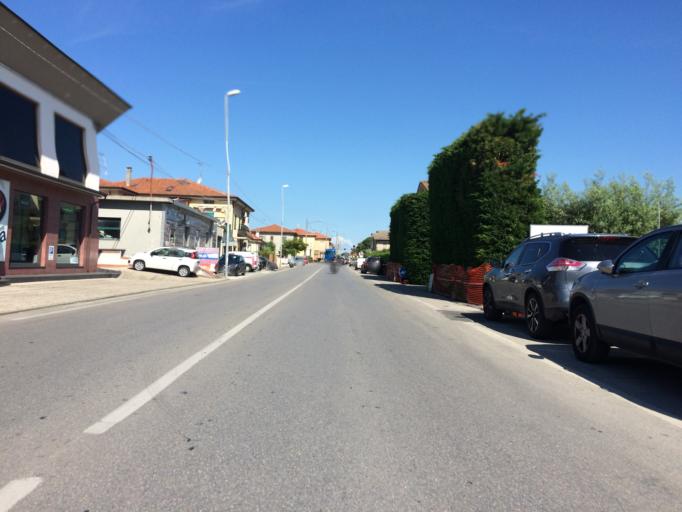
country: IT
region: Liguria
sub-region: Provincia di La Spezia
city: Casano-Dogana-Isola
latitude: 44.0647
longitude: 10.0340
